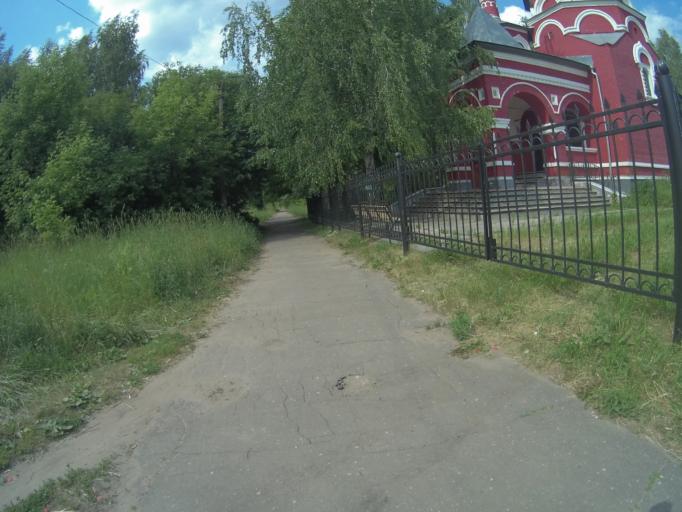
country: RU
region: Vladimir
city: Suzdal'
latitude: 56.4417
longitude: 40.4579
